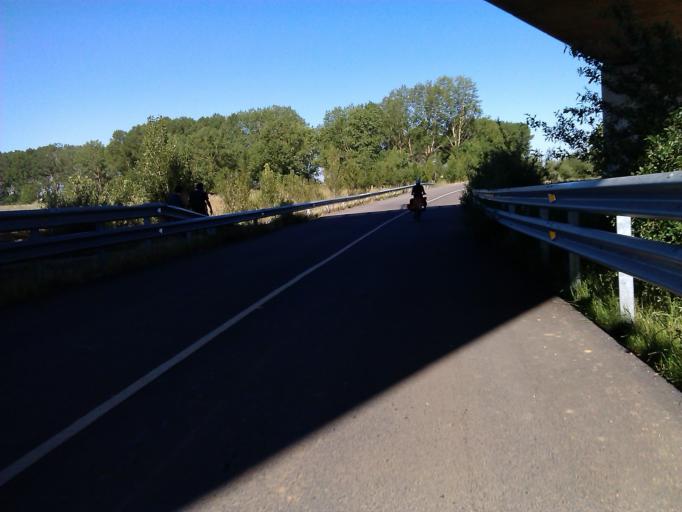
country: ES
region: Castille and Leon
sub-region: Provincia de Leon
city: Calzada del Coto
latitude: 42.3847
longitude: -5.1102
